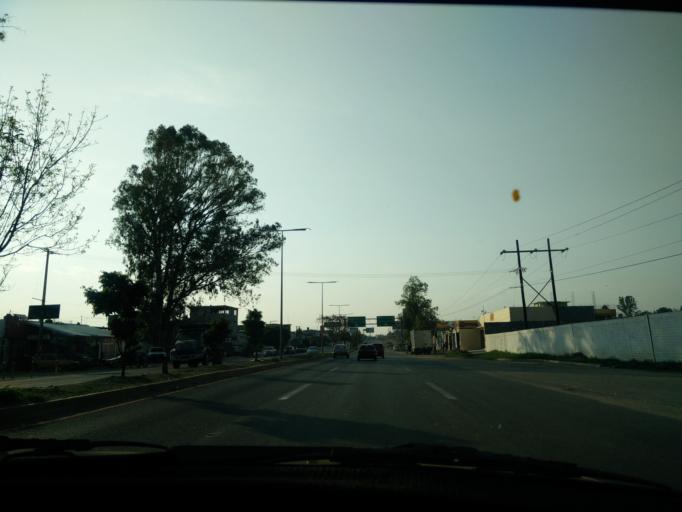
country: MX
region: Oaxaca
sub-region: Santa Maria Atzompa
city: Fraccionamiento Riberas de San Jeronimo
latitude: 17.1294
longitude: -96.7698
